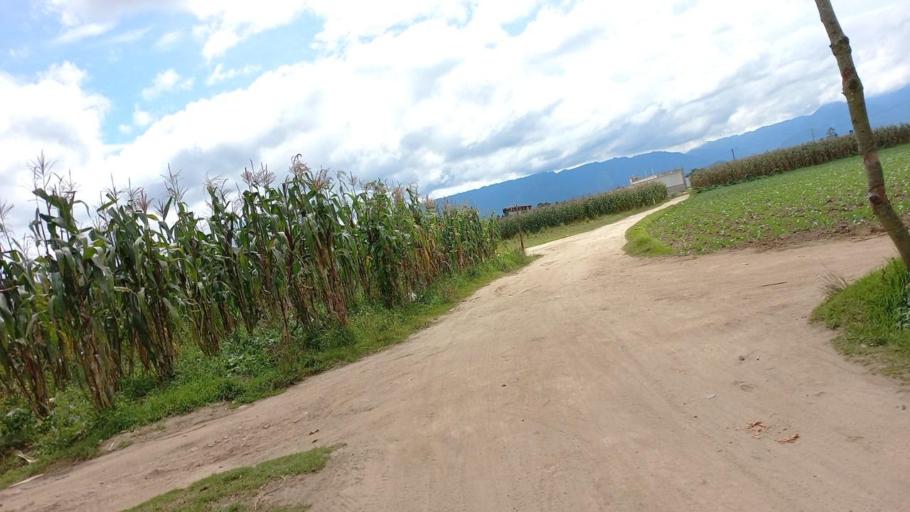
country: GT
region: Quetzaltenango
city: Salcaja
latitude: 14.8939
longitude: -91.4655
